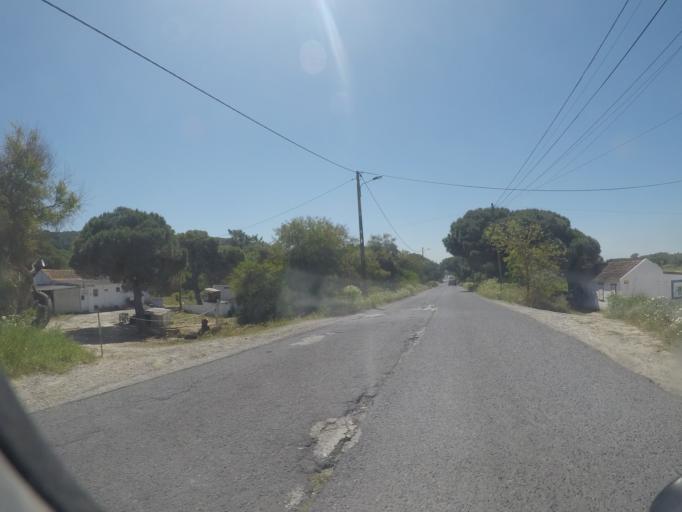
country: PT
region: Setubal
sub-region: Almada
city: Charneca
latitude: 38.6219
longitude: -9.2148
